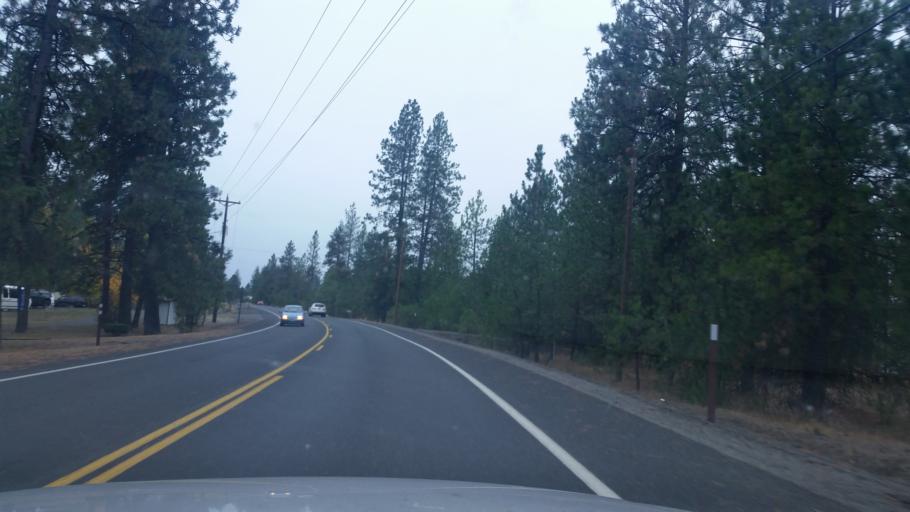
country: US
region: Washington
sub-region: Spokane County
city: Cheney
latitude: 47.5067
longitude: -117.5515
